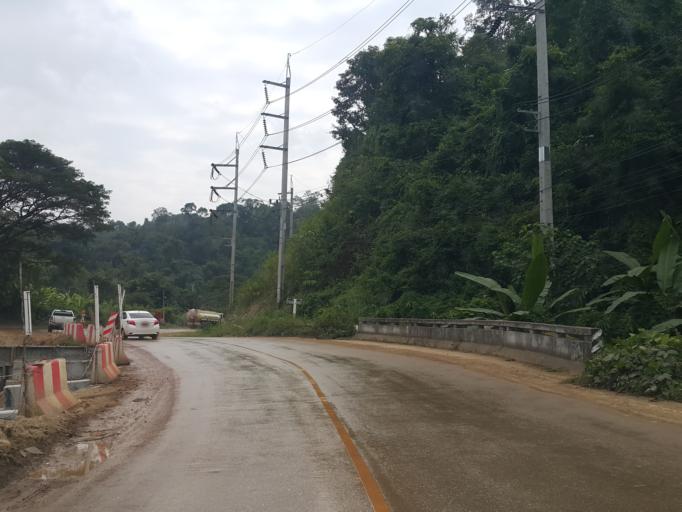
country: TH
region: Chiang Mai
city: Mae Taeng
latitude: 19.1567
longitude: 98.6922
